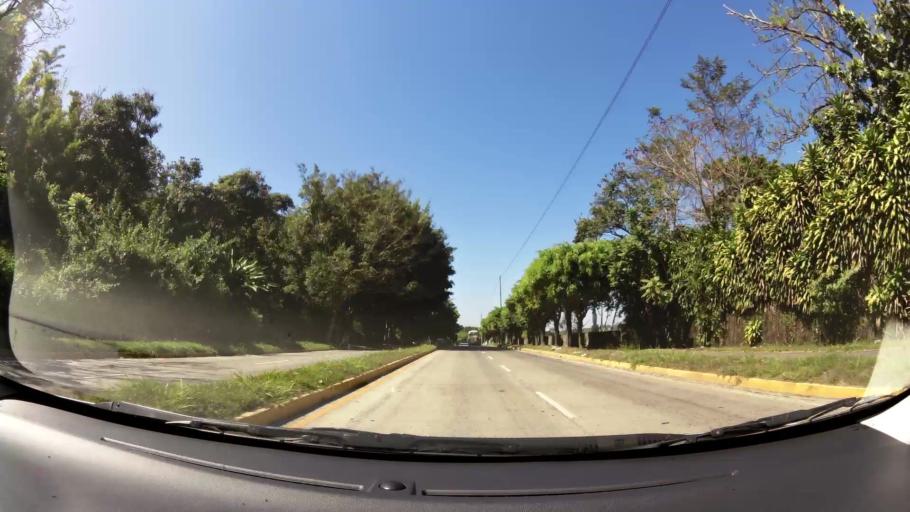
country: SV
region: La Libertad
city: Santa Tecla
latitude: 13.6679
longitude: -89.2916
